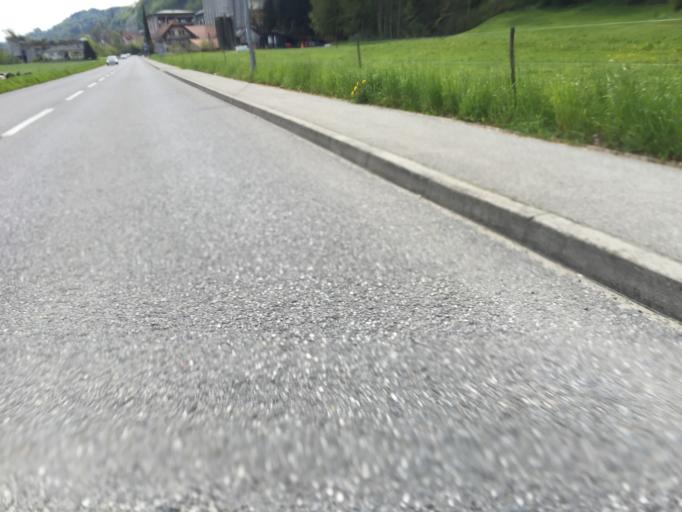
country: CH
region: Fribourg
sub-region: Sense District
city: Flamatt
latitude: 46.8910
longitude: 7.3054
